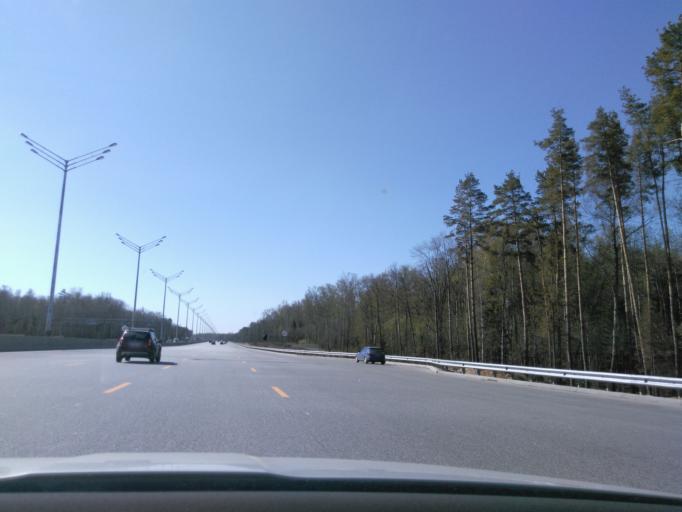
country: RU
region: Moscow
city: Khimki
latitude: 55.9326
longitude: 37.4516
